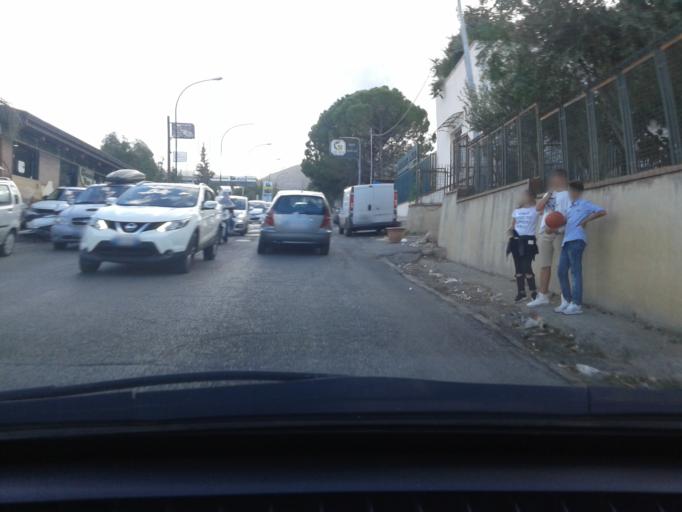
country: IT
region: Sicily
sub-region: Palermo
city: Monreale
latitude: 38.0785
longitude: 13.2951
